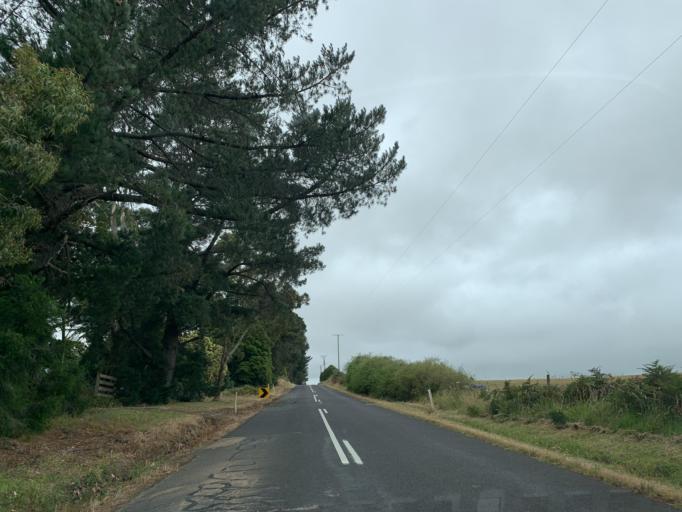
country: AU
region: Victoria
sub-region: Cardinia
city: Bunyip
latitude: -38.1801
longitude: 145.7733
